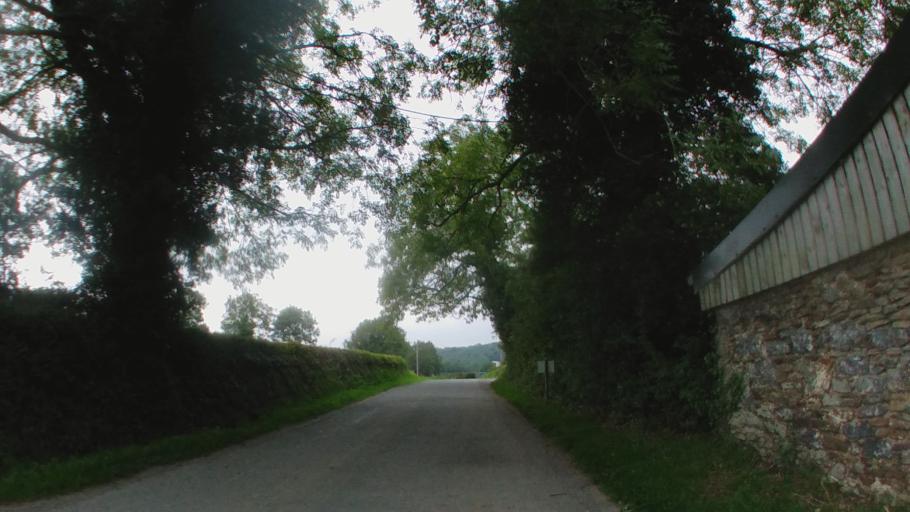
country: IE
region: Leinster
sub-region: Kilkenny
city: Kilkenny
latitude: 52.7087
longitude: -7.1945
